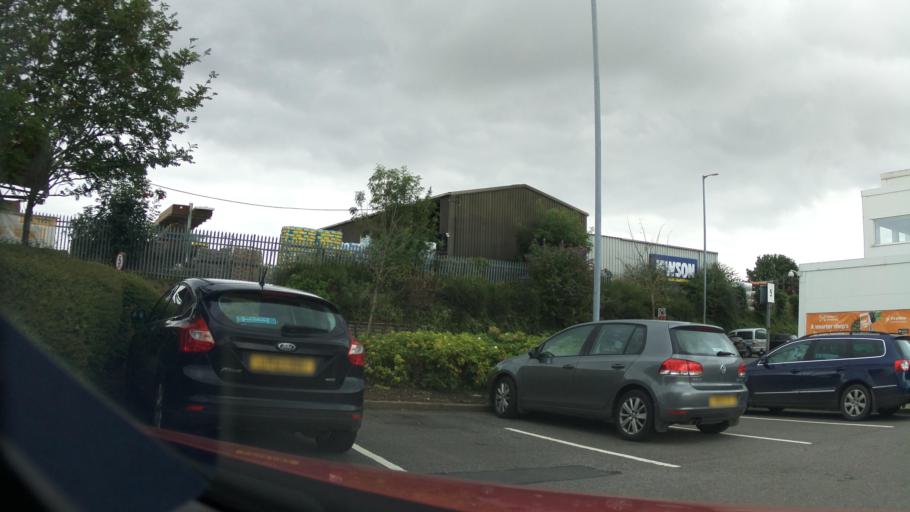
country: GB
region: England
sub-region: Lincolnshire
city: Stamford
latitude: 52.6630
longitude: -0.4657
